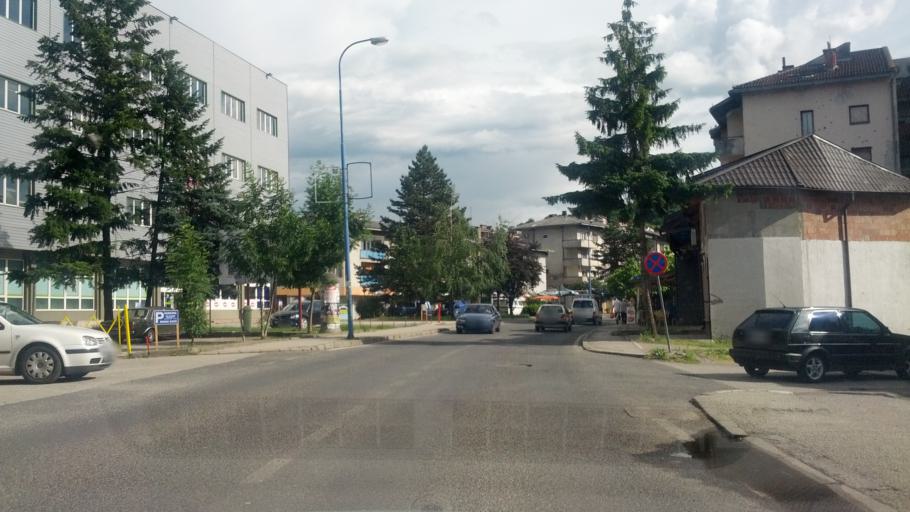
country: BA
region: Federation of Bosnia and Herzegovina
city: Bosanska Krupa
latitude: 44.8837
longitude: 16.1540
